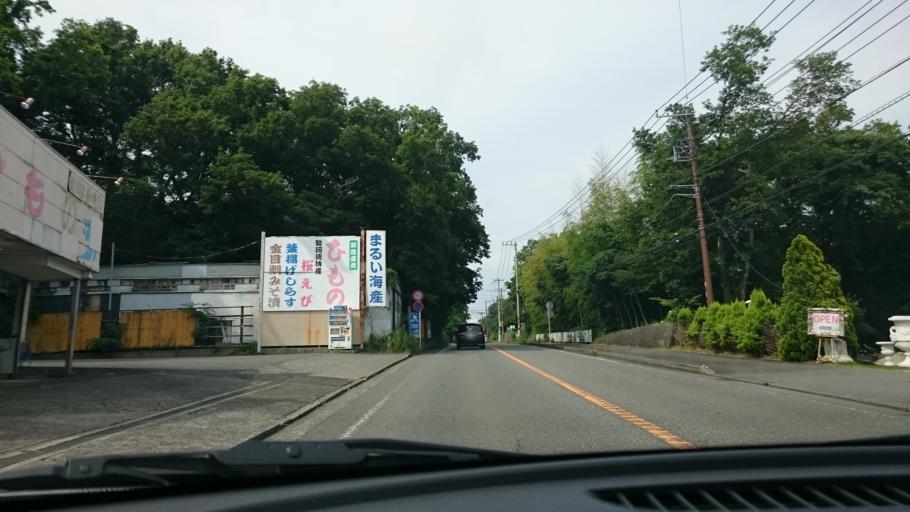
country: JP
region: Shizuoka
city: Ito
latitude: 34.8929
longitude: 139.1178
